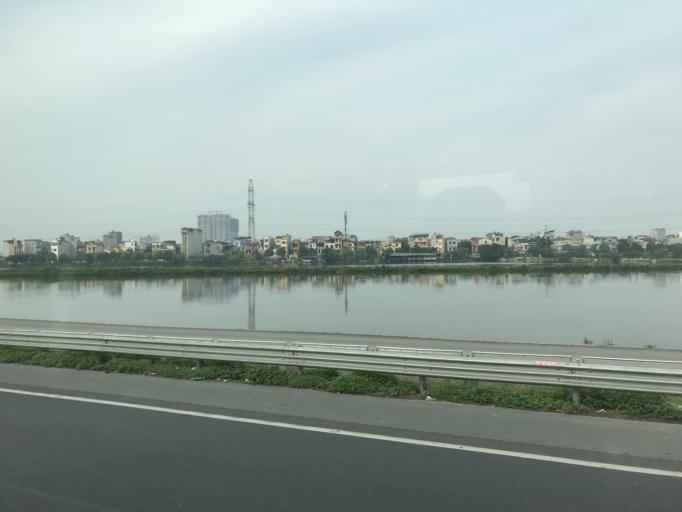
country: VN
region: Ha Noi
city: Van Dien
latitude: 20.9438
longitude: 105.8587
